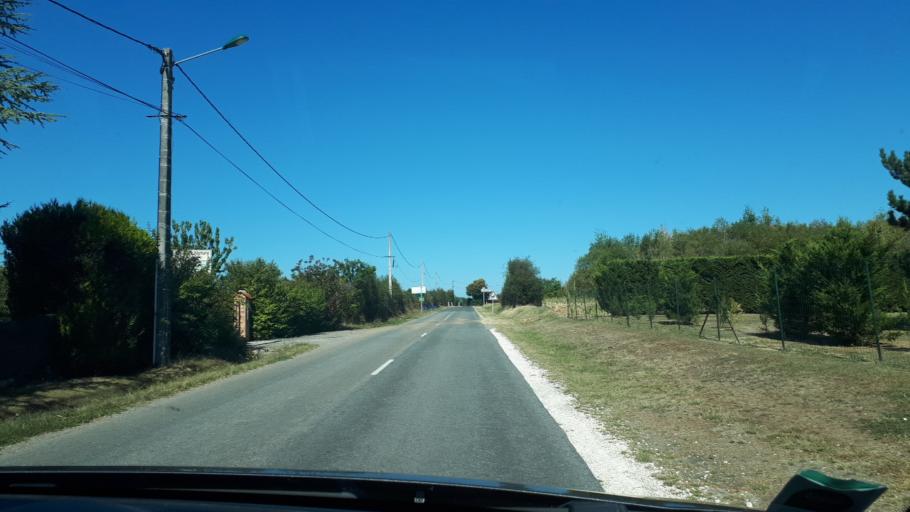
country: FR
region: Centre
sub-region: Departement du Loiret
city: Briare
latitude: 47.5880
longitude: 2.7314
